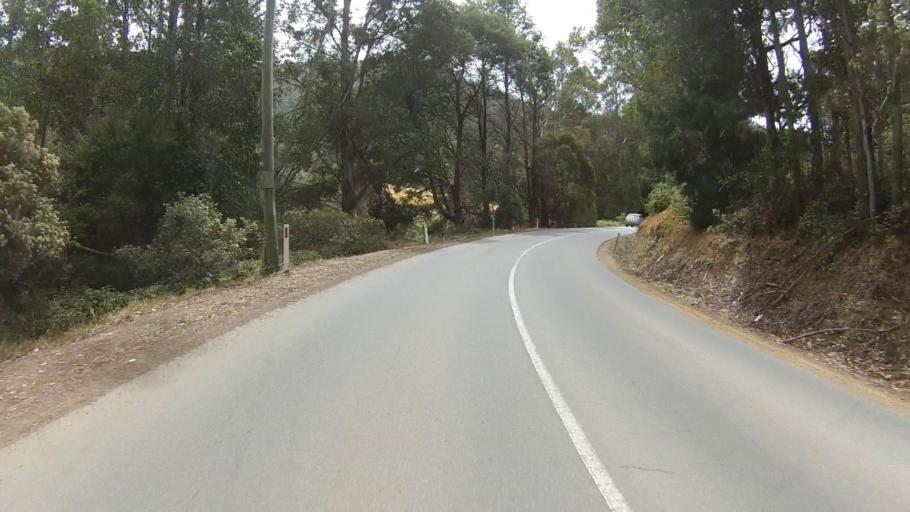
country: AU
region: Tasmania
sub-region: Kingborough
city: Kettering
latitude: -43.1075
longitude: 147.2023
